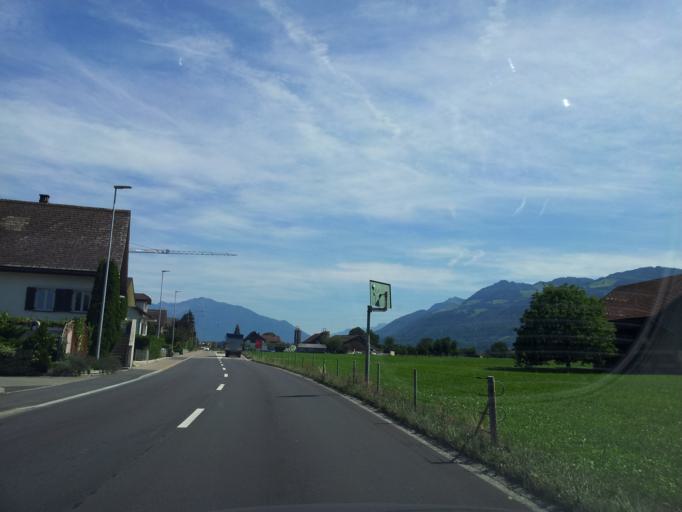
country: CH
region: Schwyz
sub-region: Bezirk March
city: Lachen
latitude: 47.1923
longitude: 8.8801
